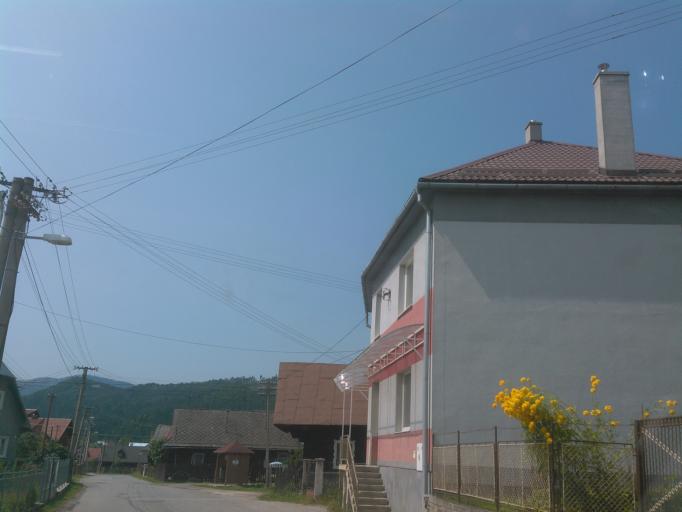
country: SK
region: Zilinsky
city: Ruzomberok
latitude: 48.9415
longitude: 19.3109
